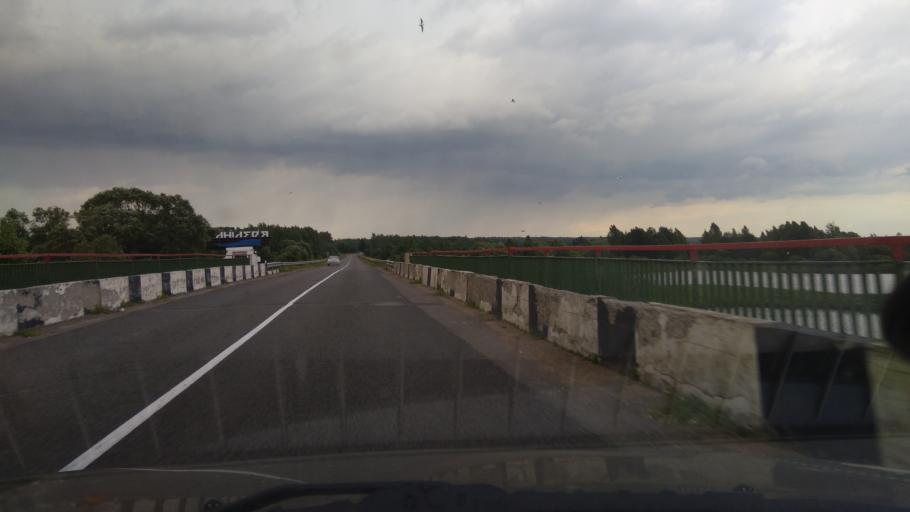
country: BY
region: Minsk
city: Il'ya
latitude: 54.4225
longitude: 27.1767
